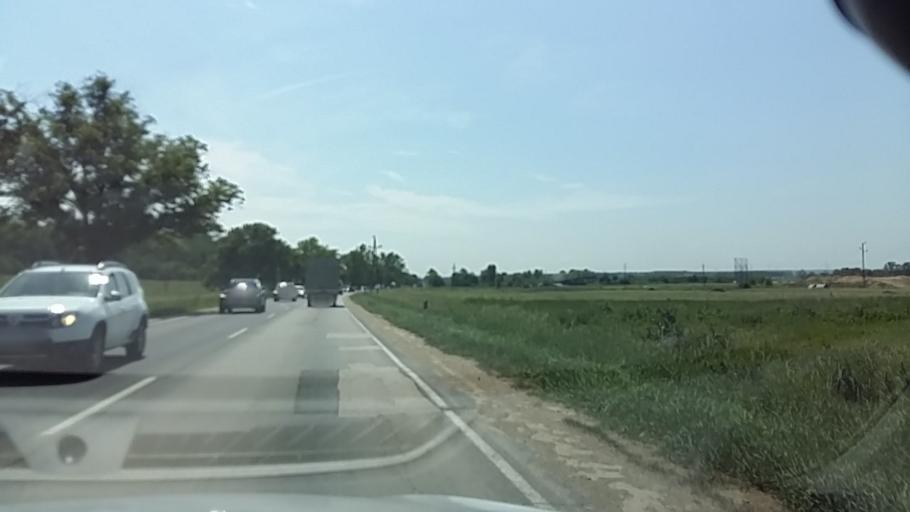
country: HU
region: Gyor-Moson-Sopron
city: Sopron
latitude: 47.6577
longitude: 16.6274
